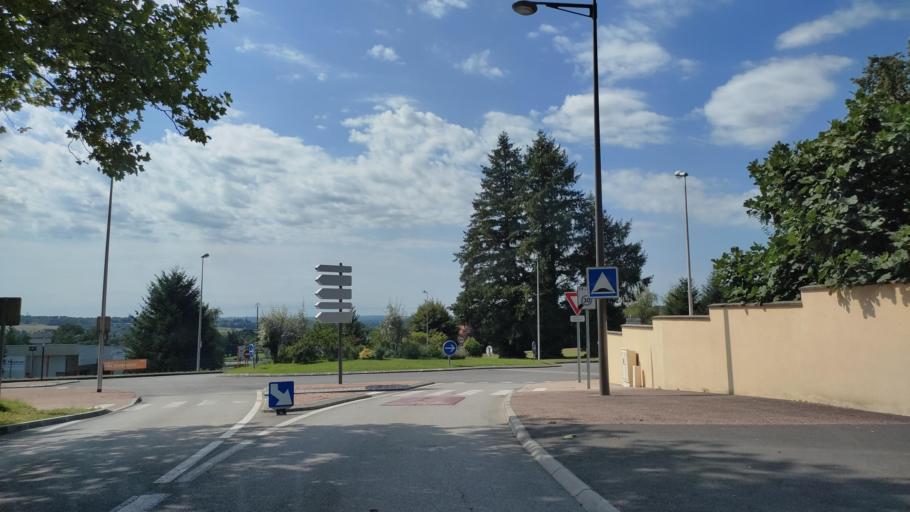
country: FR
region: Limousin
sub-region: Departement de la Haute-Vienne
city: Isle
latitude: 45.8387
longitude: 1.1947
